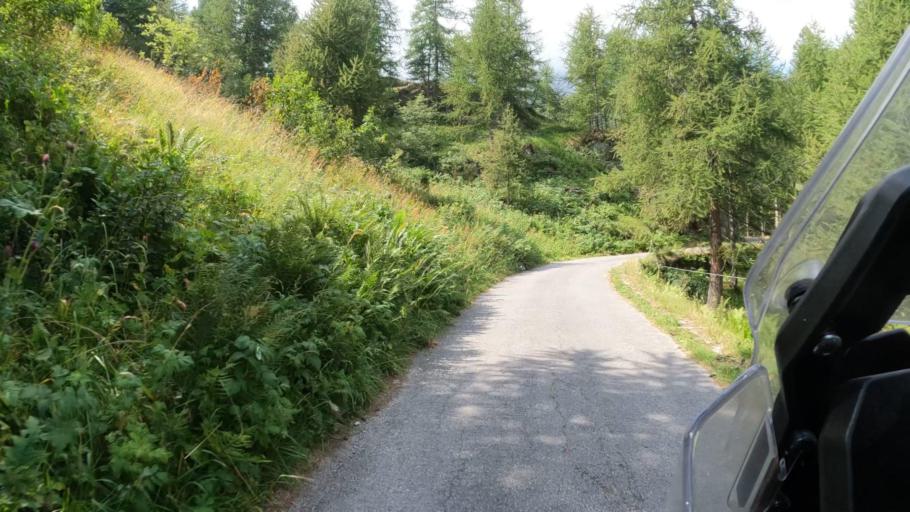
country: IT
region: Piedmont
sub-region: Provincia di Cuneo
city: Marmora
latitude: 44.4214
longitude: 7.1031
